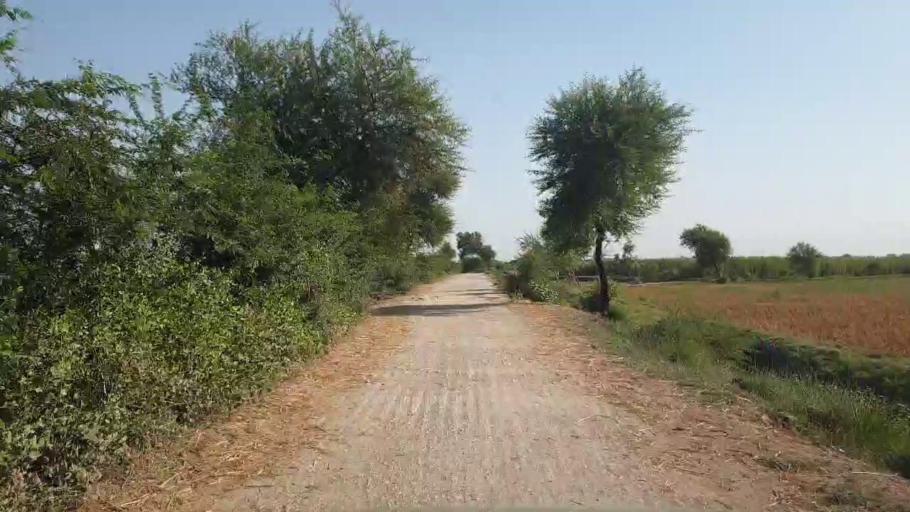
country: PK
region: Sindh
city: Matli
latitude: 25.0232
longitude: 68.7353
